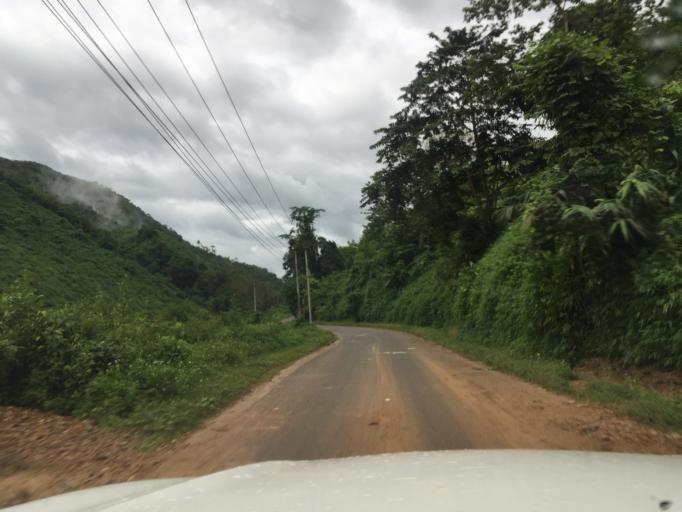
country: LA
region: Oudomxai
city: Muang La
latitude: 20.9943
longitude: 102.2303
